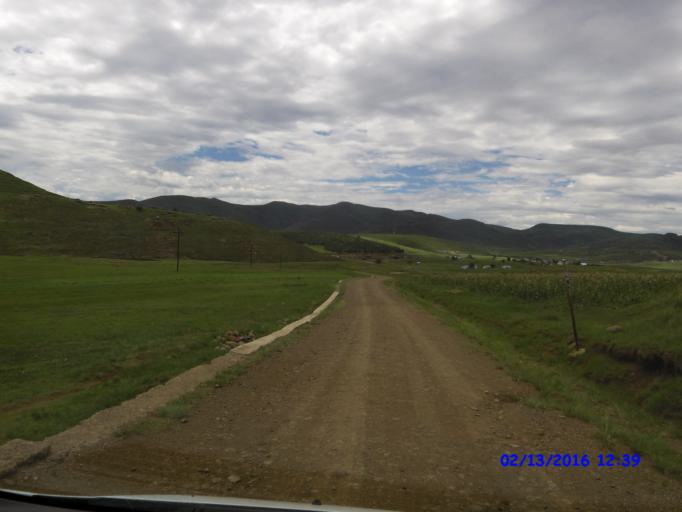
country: LS
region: Maseru
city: Nako
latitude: -29.8345
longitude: 28.0279
